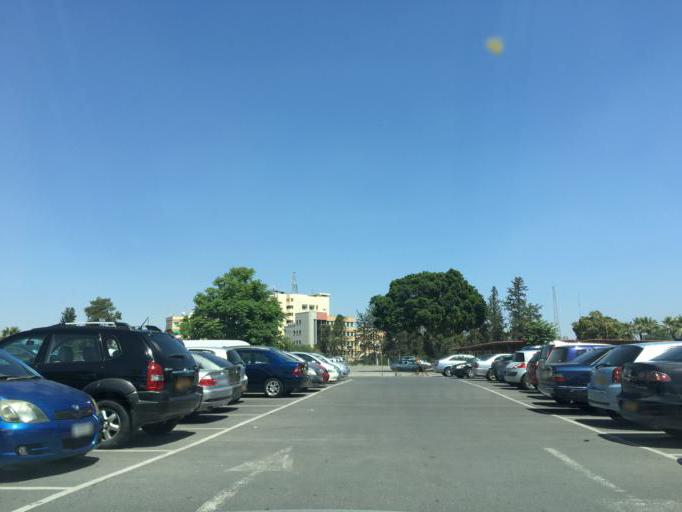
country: CY
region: Lefkosia
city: Nicosia
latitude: 35.1712
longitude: 33.3579
